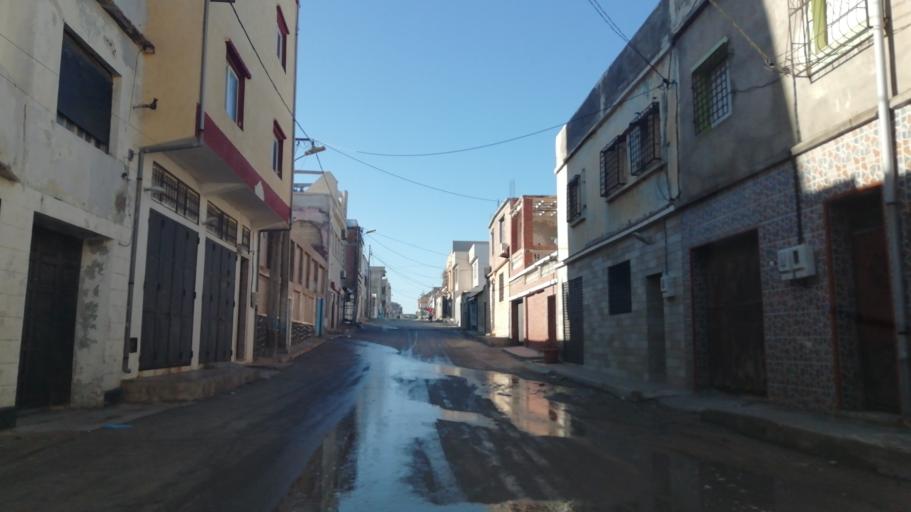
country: DZ
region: Oran
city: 'Ain el Turk
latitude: 35.7304
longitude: -0.8443
